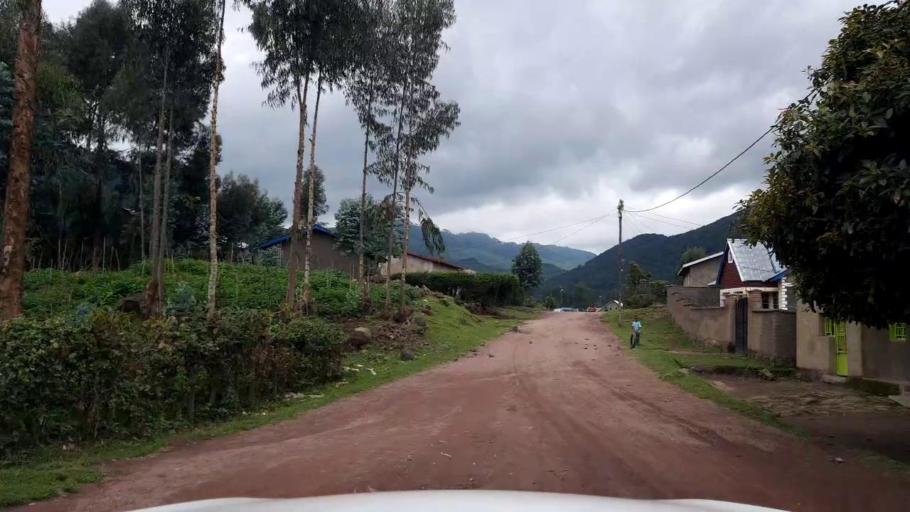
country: RW
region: Western Province
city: Gisenyi
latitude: -1.6381
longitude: 29.4066
